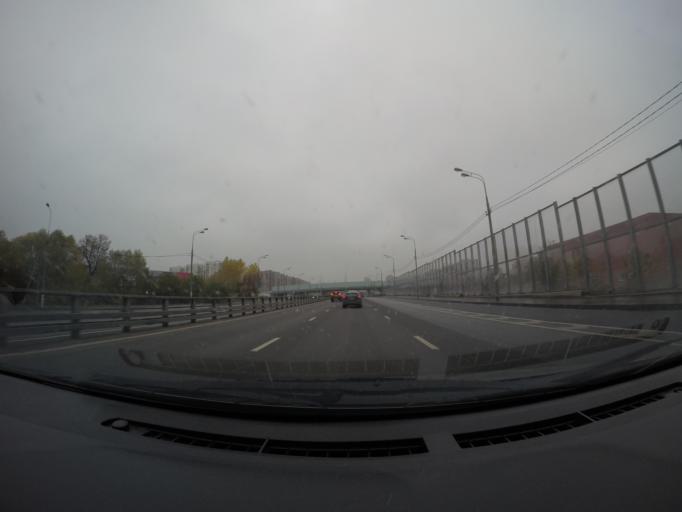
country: RU
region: Moskovskaya
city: Shcherbinka
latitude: 55.5318
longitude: 37.5814
